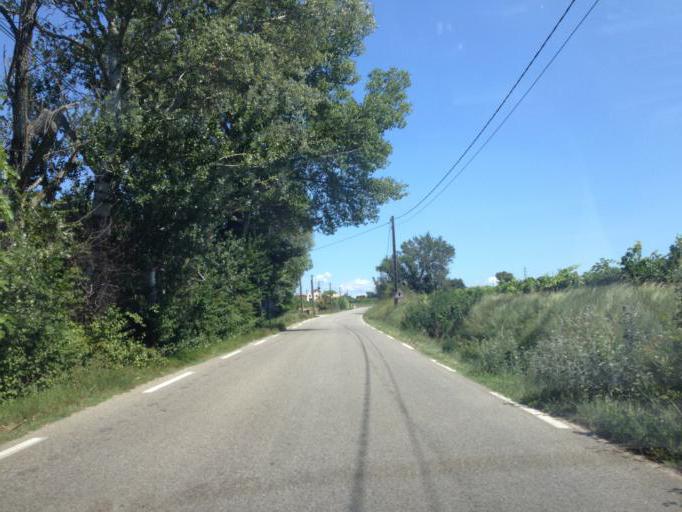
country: FR
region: Provence-Alpes-Cote d'Azur
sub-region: Departement du Vaucluse
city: Orange
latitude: 44.0959
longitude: 4.8096
